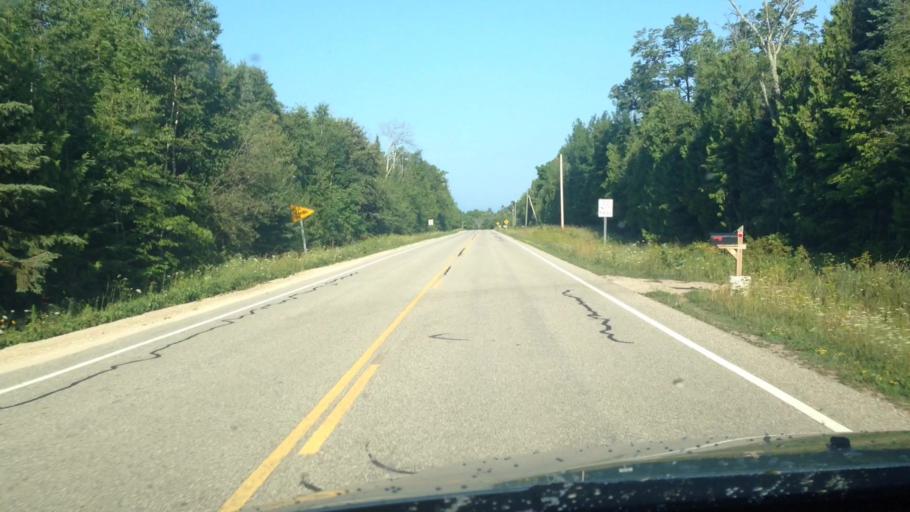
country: US
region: Michigan
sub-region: Mackinac County
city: Saint Ignace
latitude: 45.8938
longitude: -84.8159
